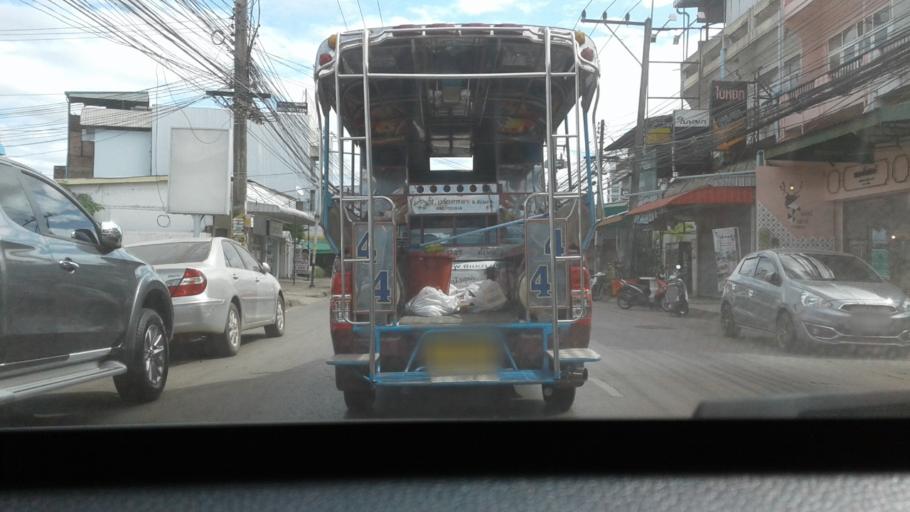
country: TH
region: Changwat Udon Thani
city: Udon Thani
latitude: 17.4087
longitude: 102.8009
